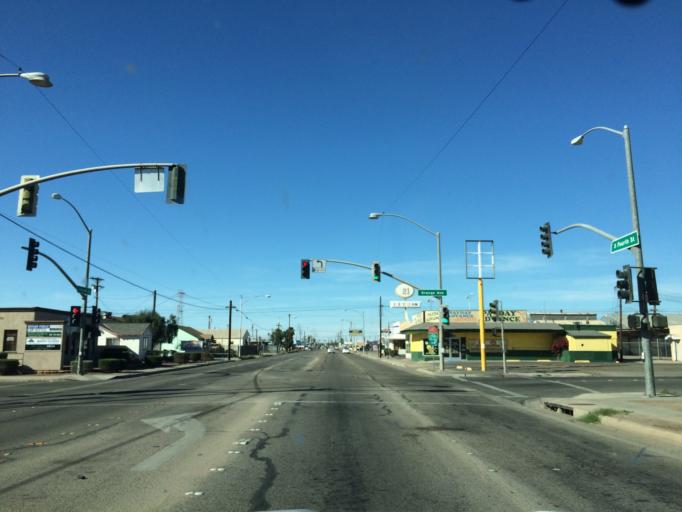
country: US
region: California
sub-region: Imperial County
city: El Centro
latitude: 32.7884
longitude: -115.5525
